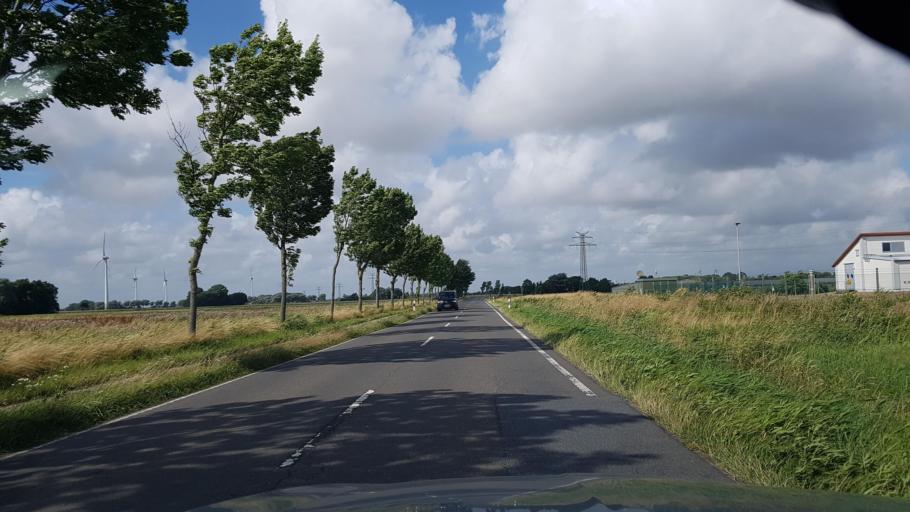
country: DE
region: Schleswig-Holstein
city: Reinsbuttel
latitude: 54.1890
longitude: 8.9028
